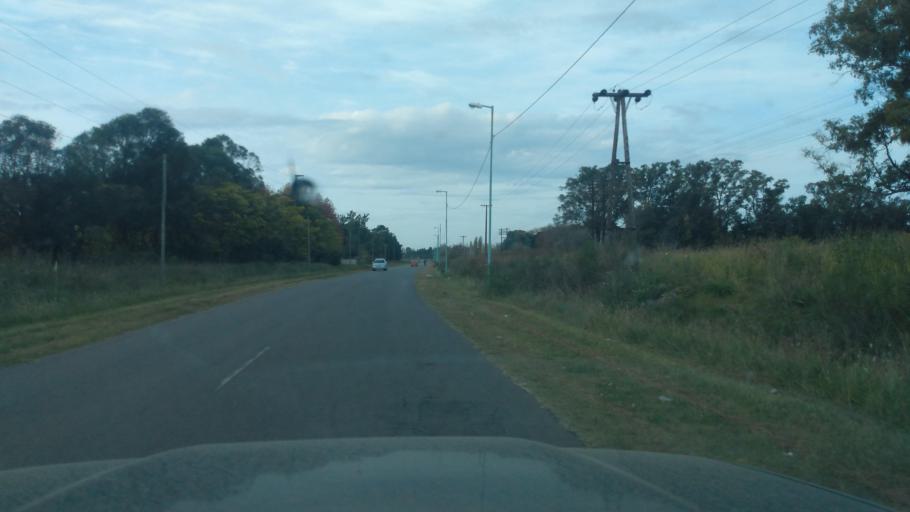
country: AR
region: Buenos Aires
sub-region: Partido de Lujan
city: Lujan
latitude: -34.5958
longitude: -59.1596
